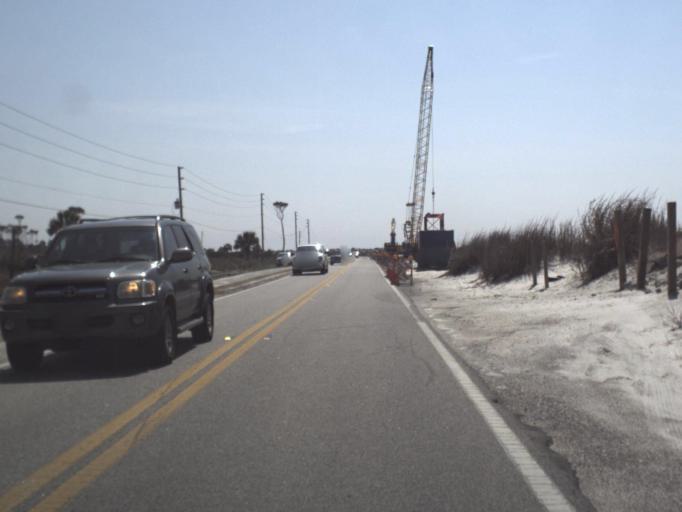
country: US
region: Florida
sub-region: Gulf County
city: Port Saint Joe
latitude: 29.6812
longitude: -85.3663
